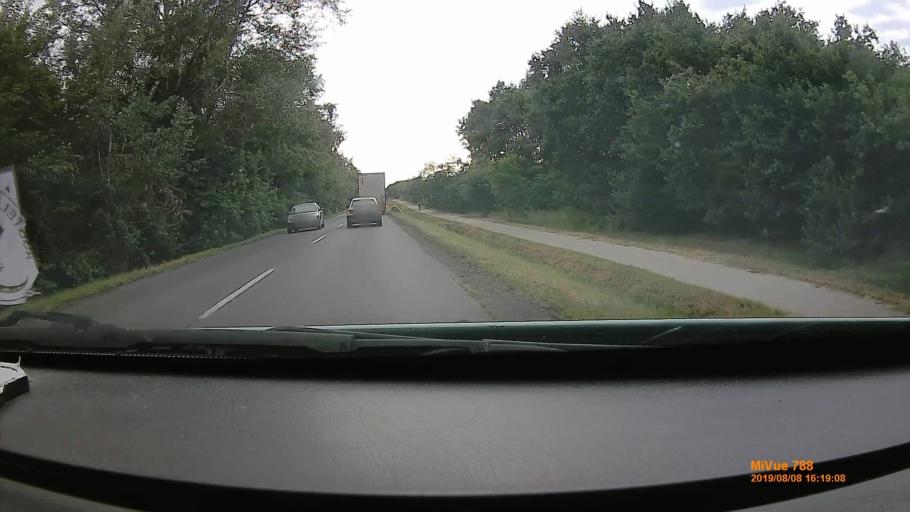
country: HU
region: Szabolcs-Szatmar-Bereg
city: Mateszalka
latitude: 47.9656
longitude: 22.2781
